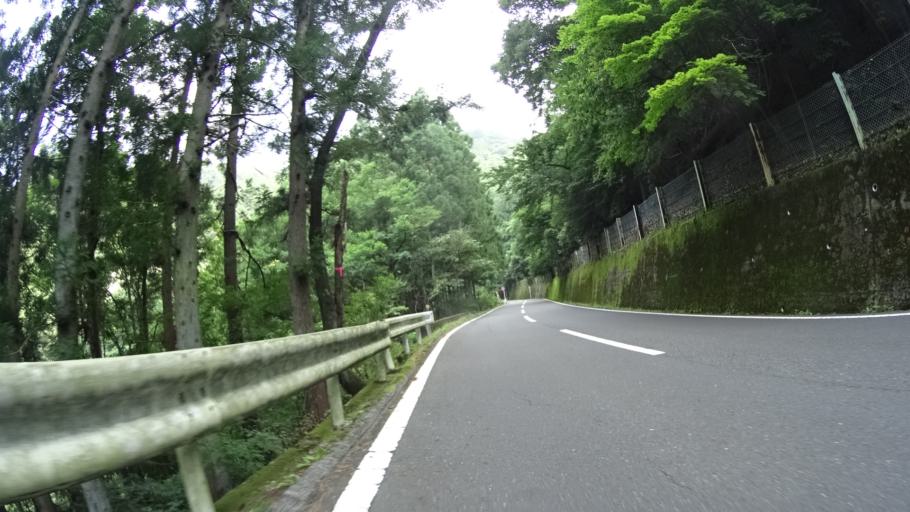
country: JP
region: Gunma
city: Tomioka
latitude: 36.0594
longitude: 138.8568
